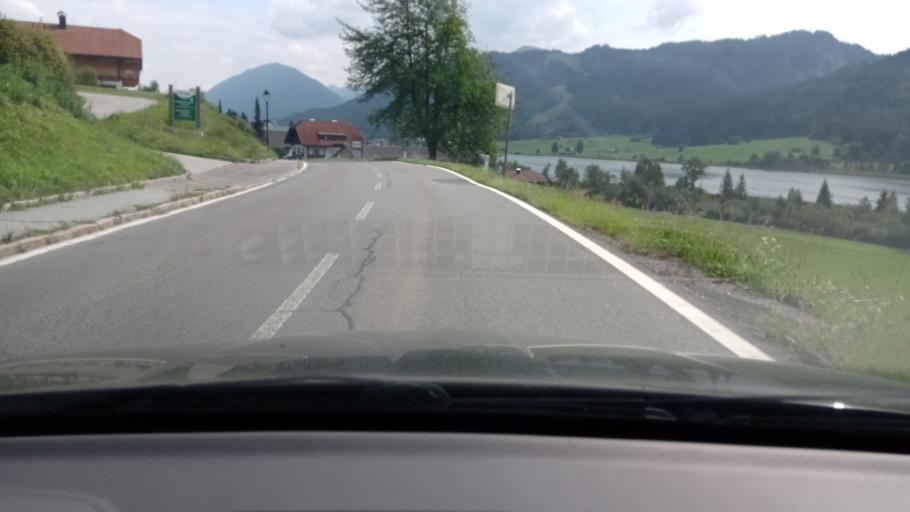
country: AT
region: Carinthia
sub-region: Politischer Bezirk Spittal an der Drau
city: Steinfeld
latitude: 46.7213
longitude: 13.2763
